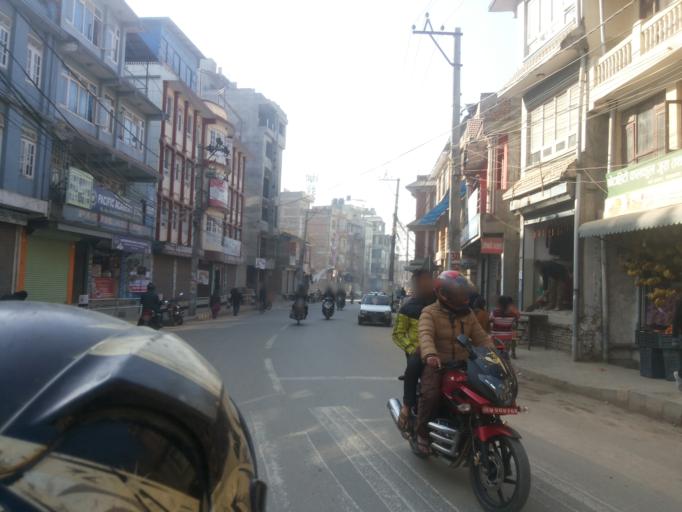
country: NP
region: Central Region
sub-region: Bagmati Zone
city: Patan
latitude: 27.6834
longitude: 85.3333
